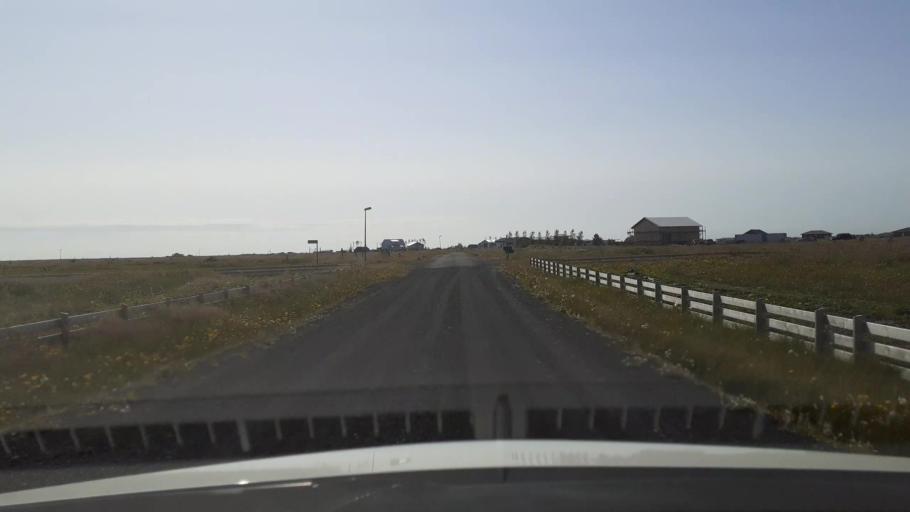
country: IS
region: South
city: Selfoss
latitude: 63.8990
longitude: -21.0812
